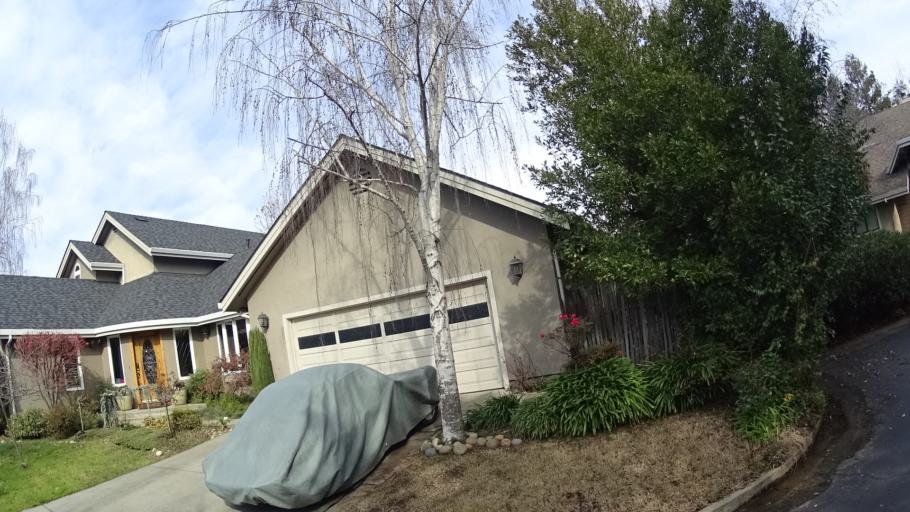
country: US
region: California
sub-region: Alameda County
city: Fairview
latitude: 37.6758
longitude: -122.0532
